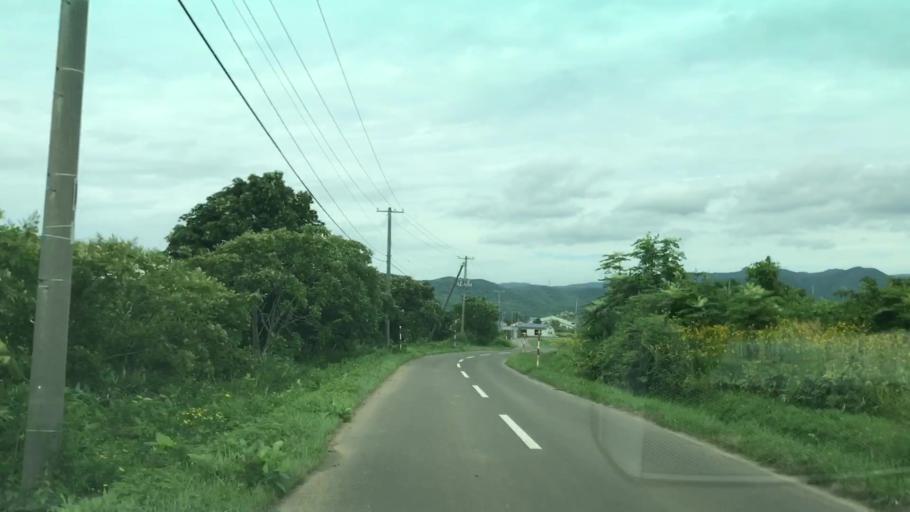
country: JP
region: Hokkaido
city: Iwanai
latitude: 43.0255
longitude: 140.5694
